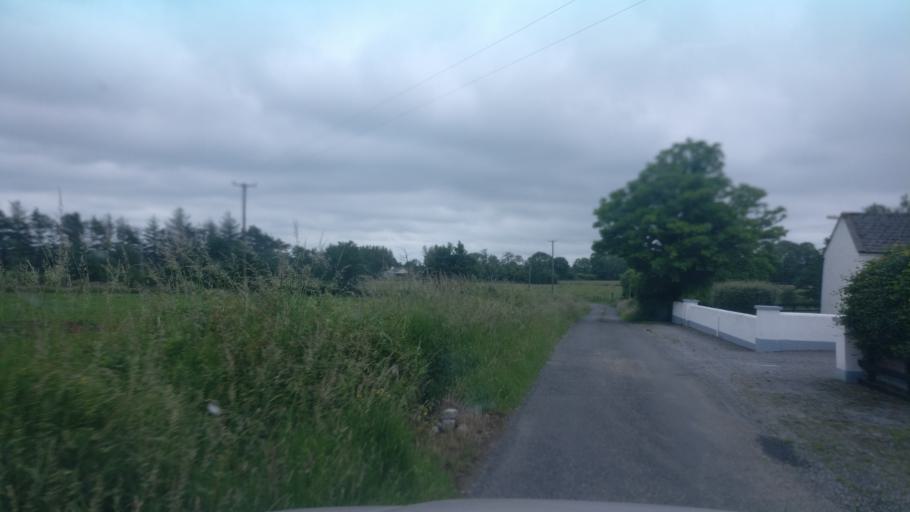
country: IE
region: Connaught
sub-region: County Galway
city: Ballinasloe
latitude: 53.3041
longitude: -8.3513
